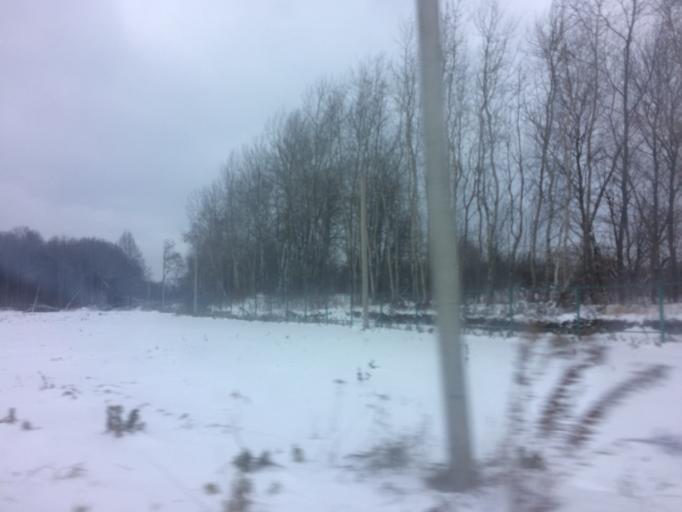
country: RU
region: Tula
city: Mendeleyevskiy
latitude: 54.1419
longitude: 37.6397
